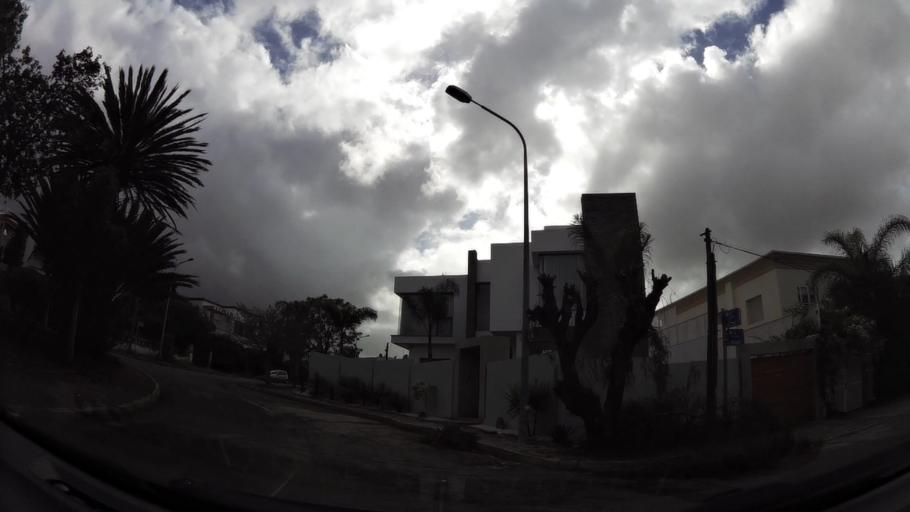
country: MA
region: Grand Casablanca
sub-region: Casablanca
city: Casablanca
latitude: 33.5524
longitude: -7.6193
